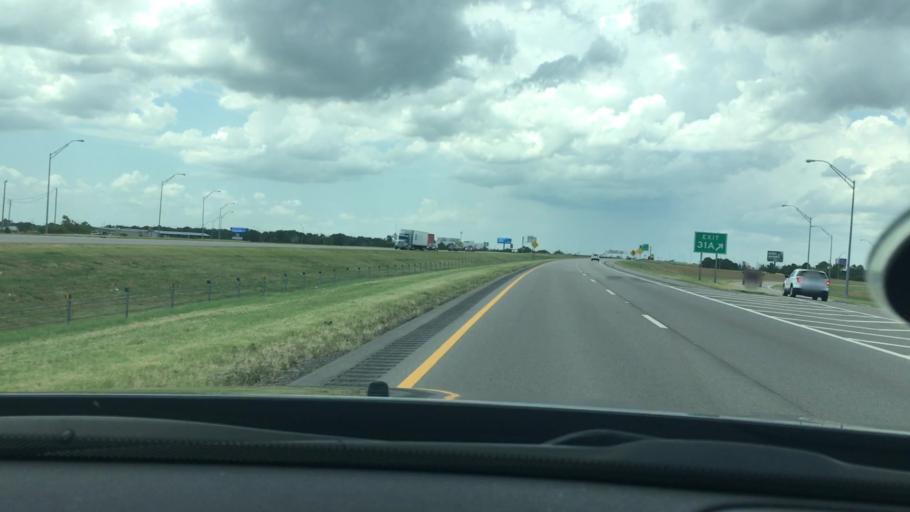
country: US
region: Oklahoma
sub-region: Carter County
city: Ardmore
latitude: 34.1684
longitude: -97.1675
